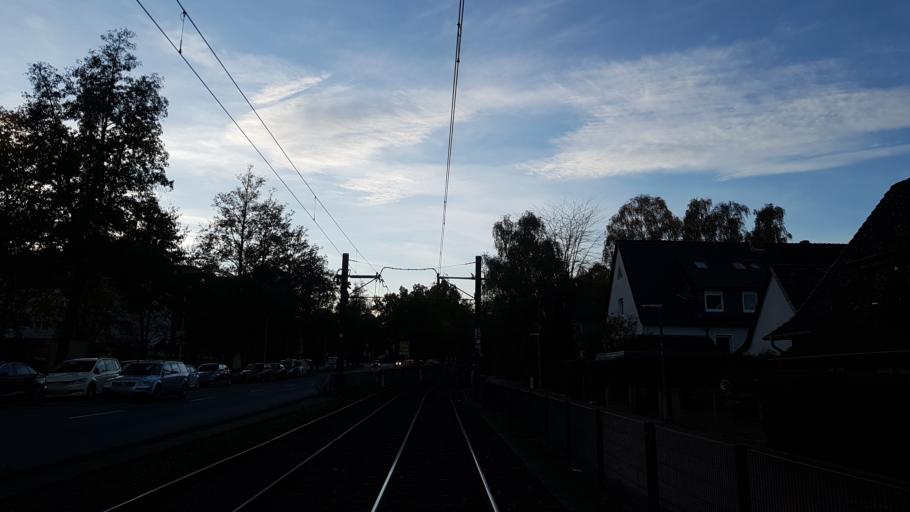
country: DE
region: Lower Saxony
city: Hemmingen
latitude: 52.3415
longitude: 9.7007
